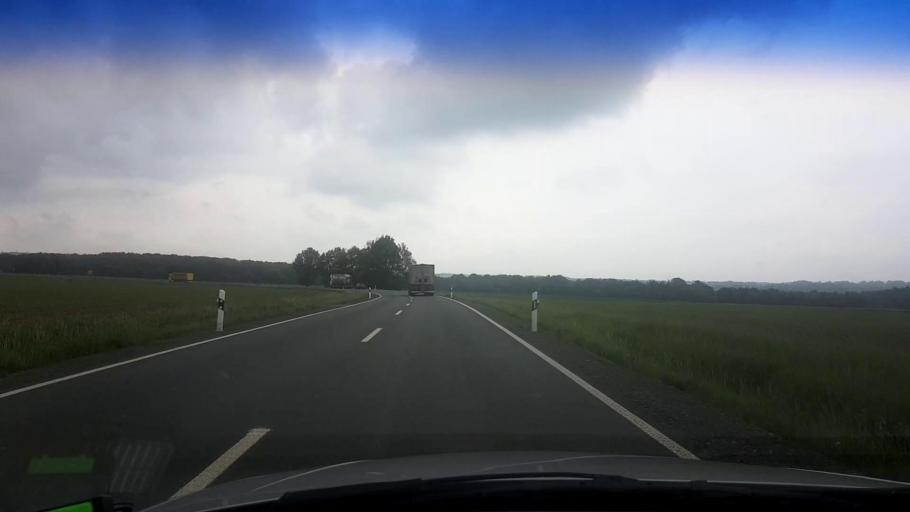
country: DE
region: Bavaria
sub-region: Upper Franconia
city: Gesees
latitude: 50.0197
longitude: 11.6641
